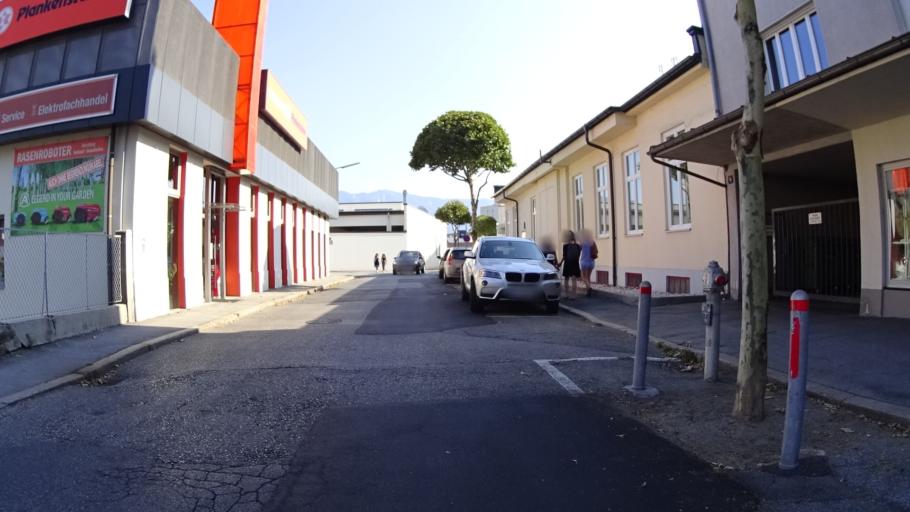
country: AT
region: Carinthia
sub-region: Villach Stadt
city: Villach
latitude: 46.6172
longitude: 13.8517
